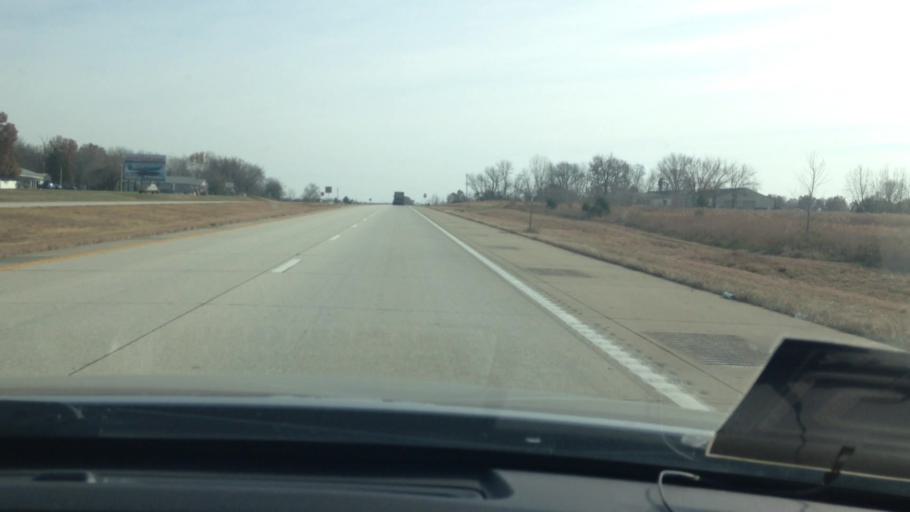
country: US
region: Missouri
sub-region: Henry County
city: Clinton
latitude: 38.4360
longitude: -93.9388
